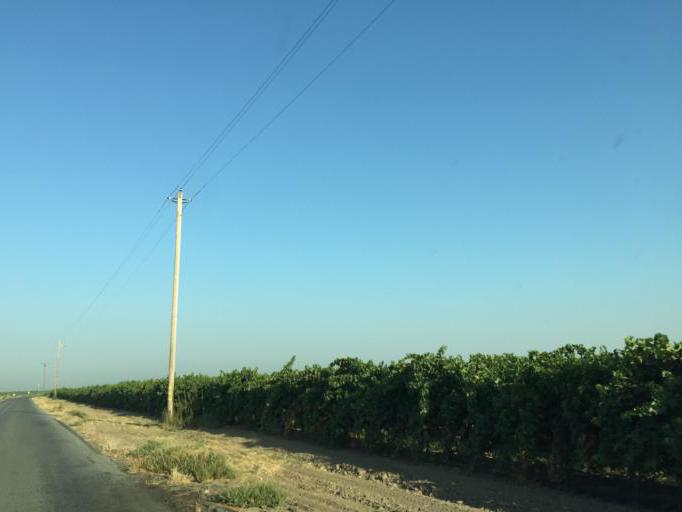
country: US
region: California
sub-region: Tulare County
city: London
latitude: 36.4582
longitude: -119.4183
